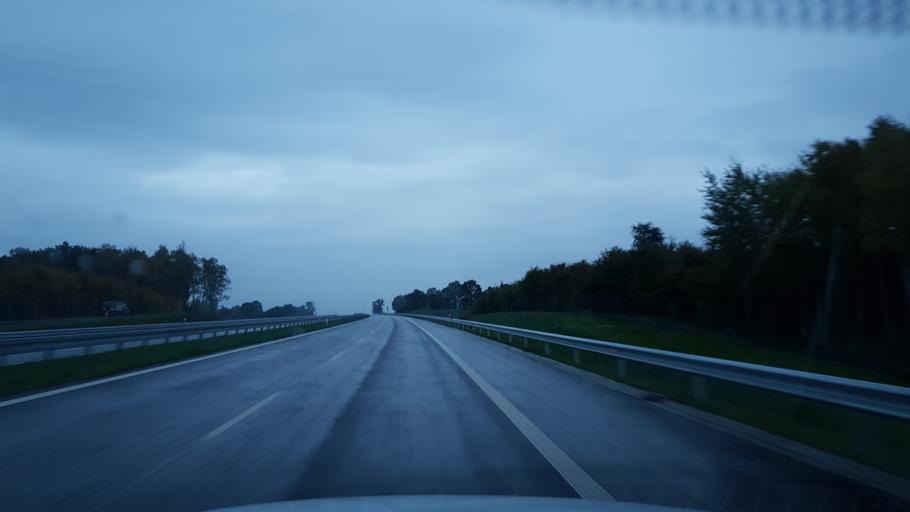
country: PL
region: West Pomeranian Voivodeship
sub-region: Powiat kolobrzeski
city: Ryman
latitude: 54.0122
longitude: 15.4738
